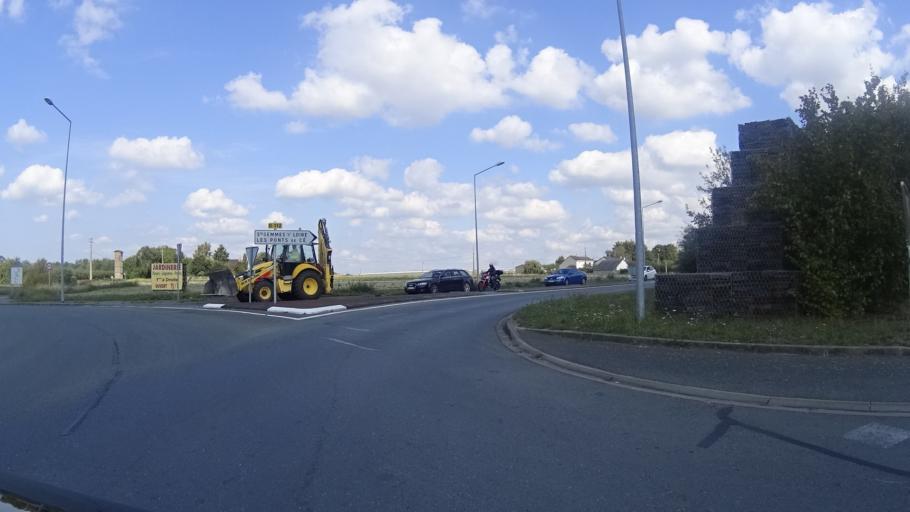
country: FR
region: Pays de la Loire
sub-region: Departement de Maine-et-Loire
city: Sainte-Gemmes-sur-Loire
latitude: 47.4203
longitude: -0.5819
